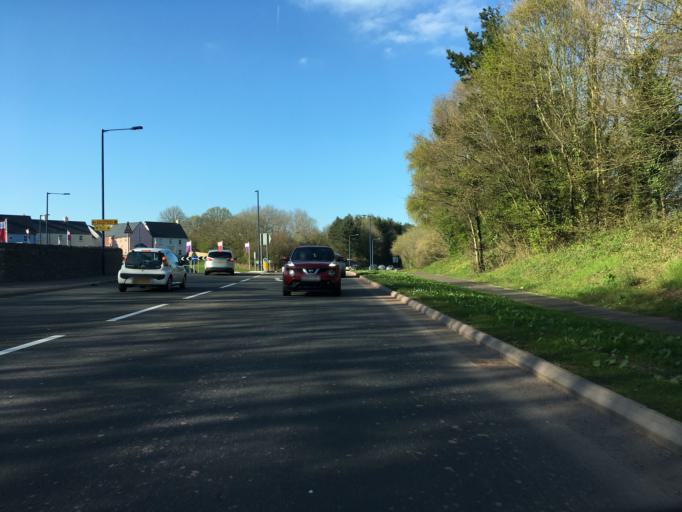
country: GB
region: Wales
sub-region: Torfaen County Borough
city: Cwmbran
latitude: 51.6698
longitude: -3.0220
